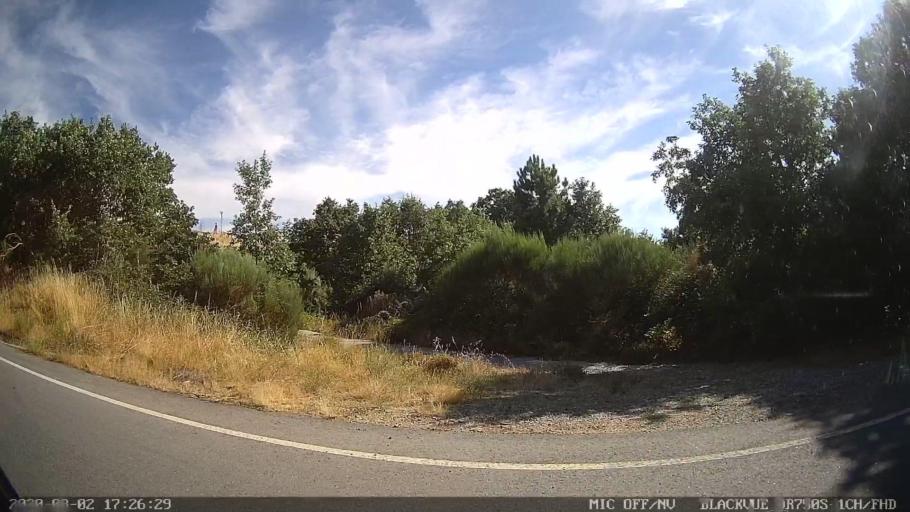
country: PT
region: Vila Real
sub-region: Sabrosa
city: Sabrosa
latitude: 41.3609
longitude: -7.5929
